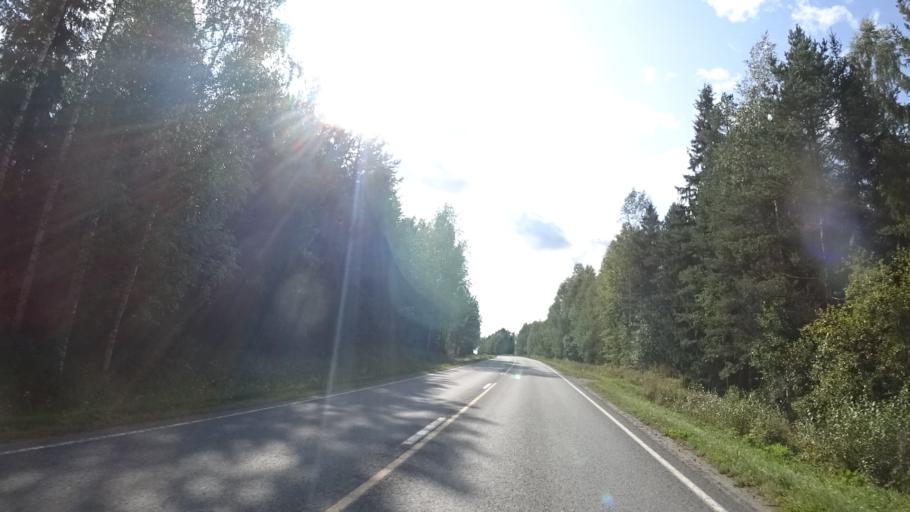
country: FI
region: North Karelia
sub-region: Keski-Karjala
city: Kitee
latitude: 62.0960
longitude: 30.0729
